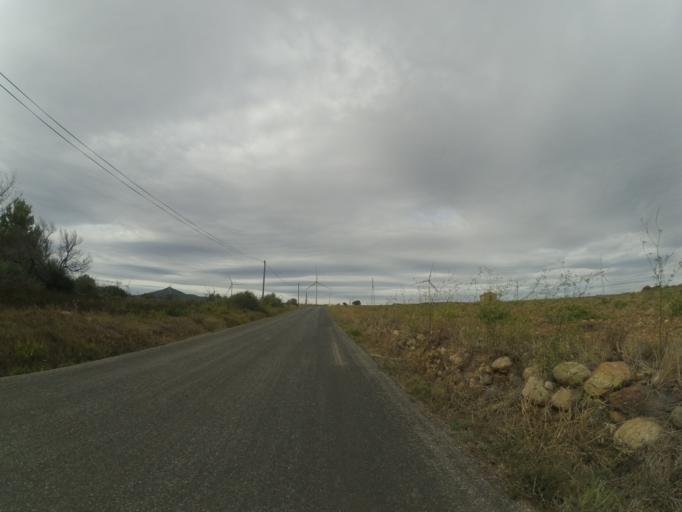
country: FR
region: Languedoc-Roussillon
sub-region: Departement des Pyrenees-Orientales
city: Pezilla-la-Riviere
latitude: 42.7112
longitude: 2.7588
